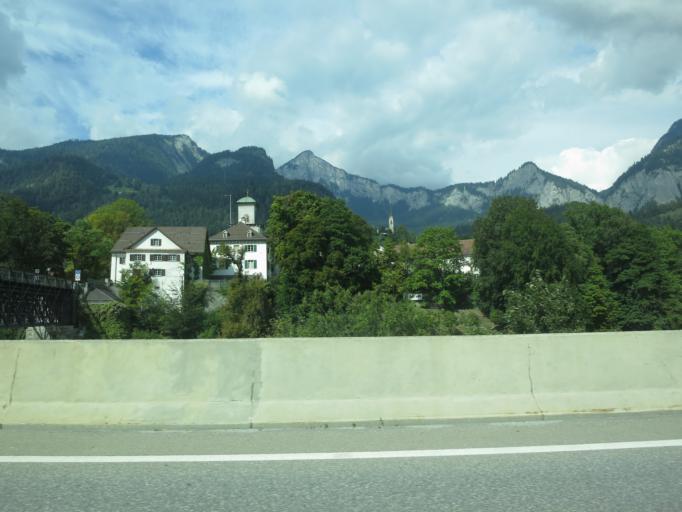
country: CH
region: Grisons
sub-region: Imboden District
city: Tamins
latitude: 46.8235
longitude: 9.4104
